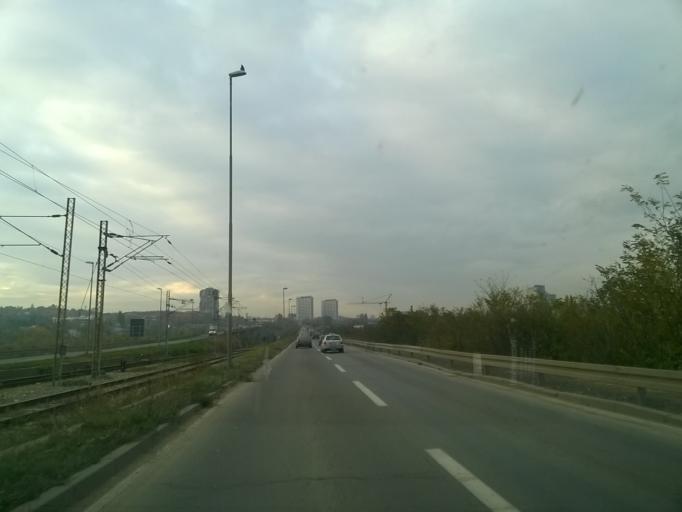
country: RS
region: Central Serbia
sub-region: Belgrade
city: Palilula
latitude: 44.8236
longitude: 20.4909
